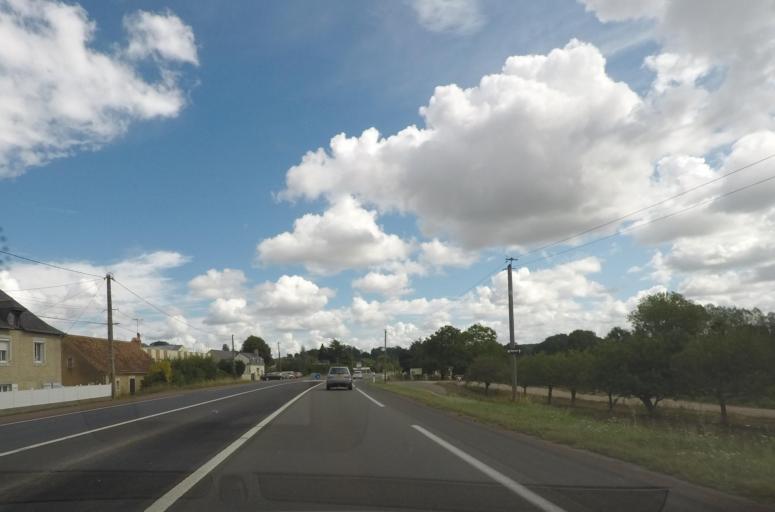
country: FR
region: Pays de la Loire
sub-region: Departement de la Sarthe
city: Clermont-Creans
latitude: 47.7116
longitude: -0.0366
